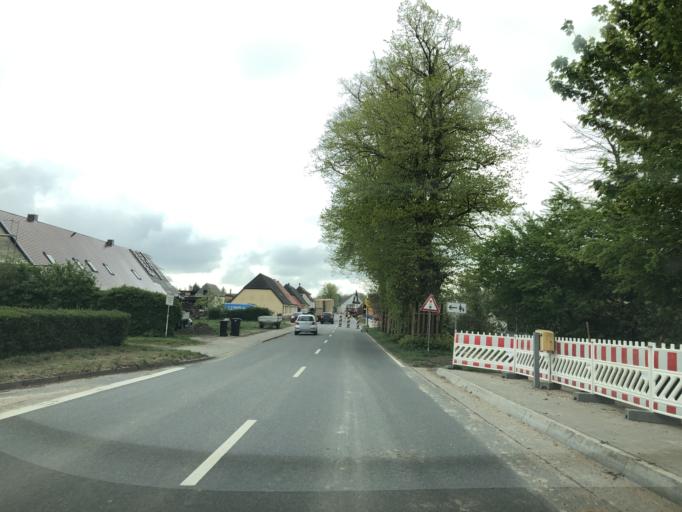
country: DE
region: Mecklenburg-Vorpommern
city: Guestrow
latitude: 53.7165
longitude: 12.1375
